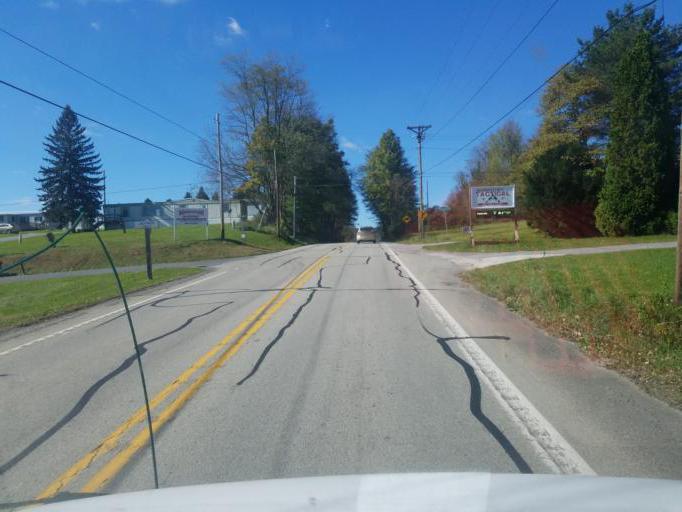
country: US
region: Pennsylvania
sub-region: Somerset County
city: Boswell
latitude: 40.1640
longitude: -79.0811
